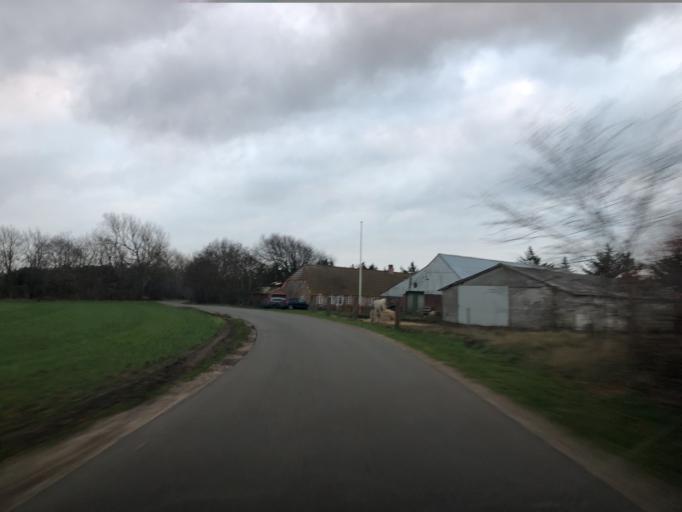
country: DK
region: Central Jutland
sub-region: Holstebro Kommune
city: Ulfborg
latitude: 56.2336
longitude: 8.2766
